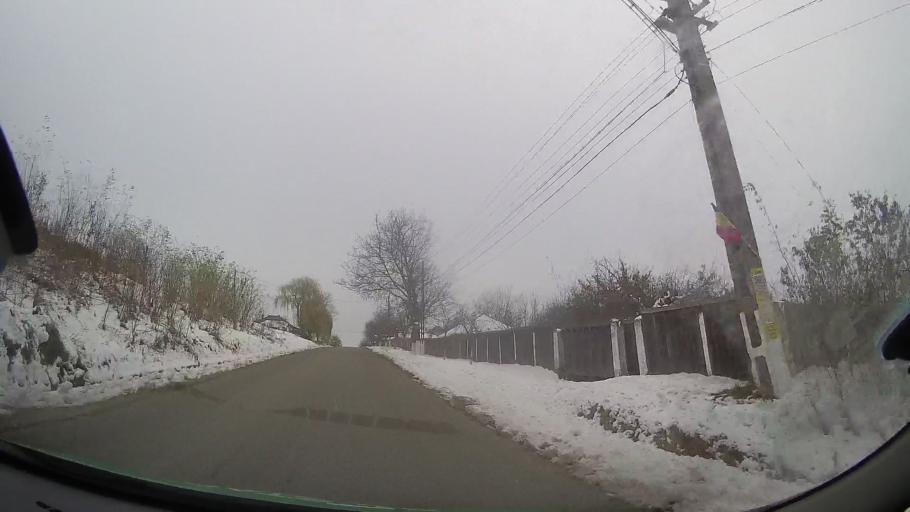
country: RO
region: Bacau
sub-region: Comuna Huruesti
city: Huruesti
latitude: 46.3045
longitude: 27.2946
